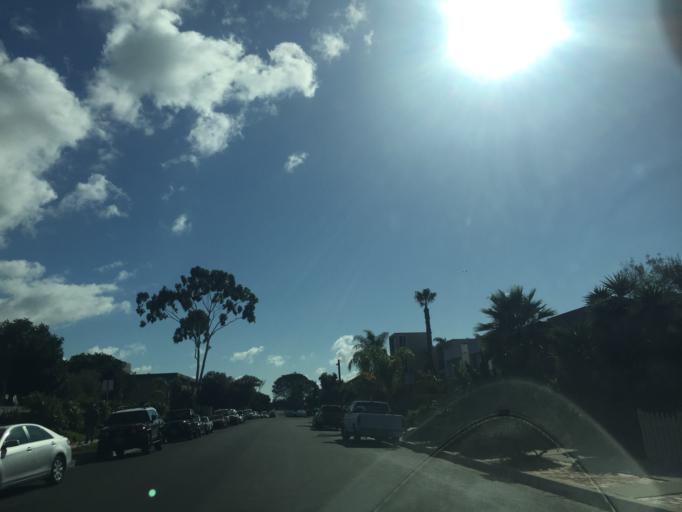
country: US
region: California
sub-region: San Diego County
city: La Jolla
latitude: 32.7911
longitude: -117.2402
